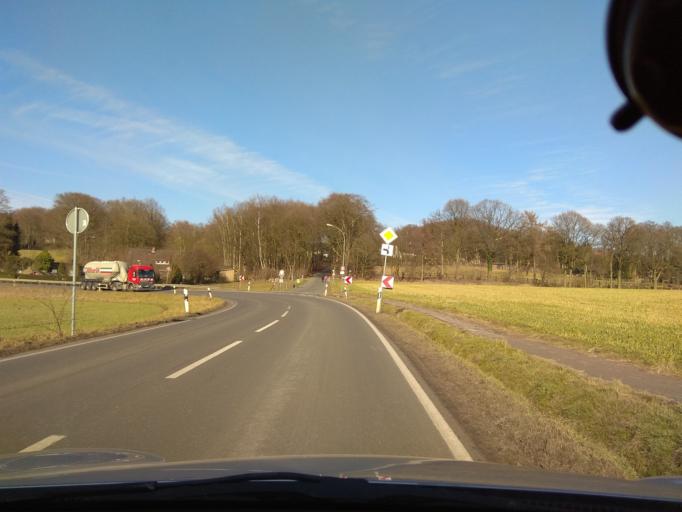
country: DE
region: North Rhine-Westphalia
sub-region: Regierungsbezirk Munster
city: Mettingen
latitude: 52.2725
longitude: 7.7897
